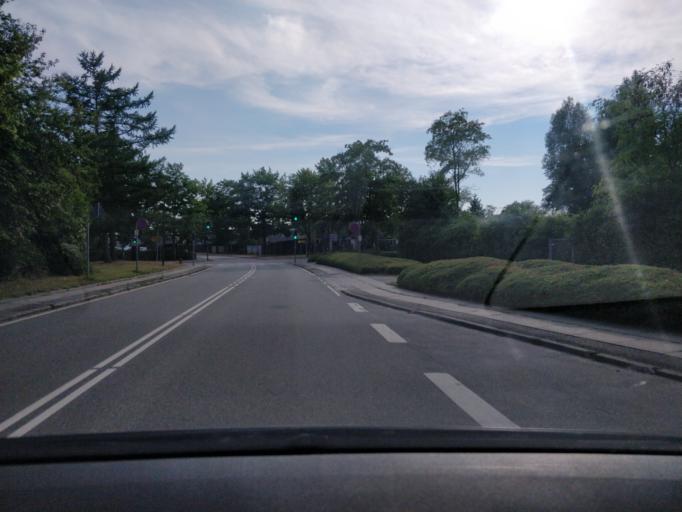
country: DK
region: Capital Region
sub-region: Herlev Kommune
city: Herlev
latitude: 55.7316
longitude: 12.4257
